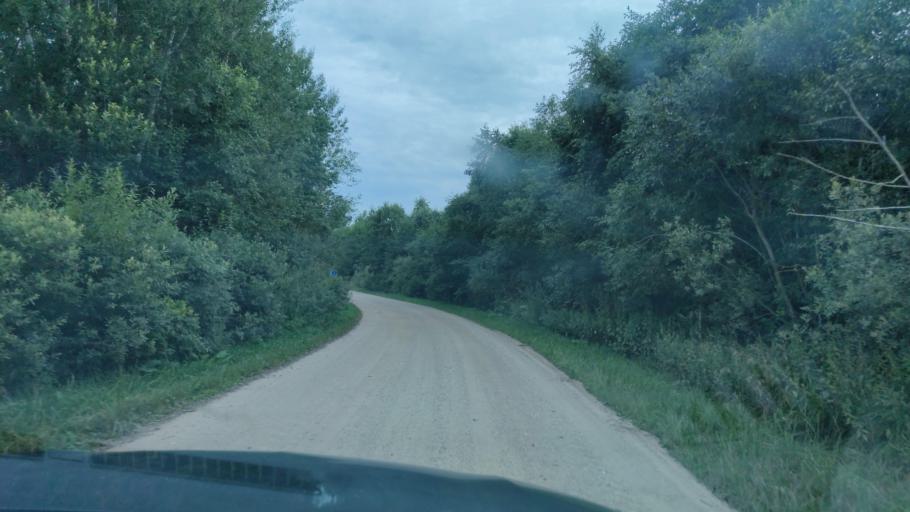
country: BY
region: Vitebsk
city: Pastavy
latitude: 55.1149
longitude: 27.1467
